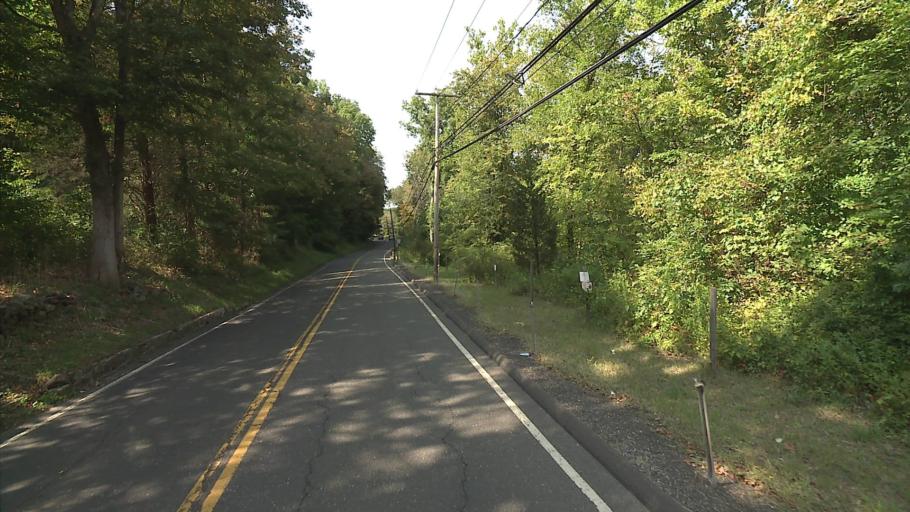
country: US
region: Connecticut
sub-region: New Haven County
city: Heritage Village
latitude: 41.4637
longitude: -73.2445
